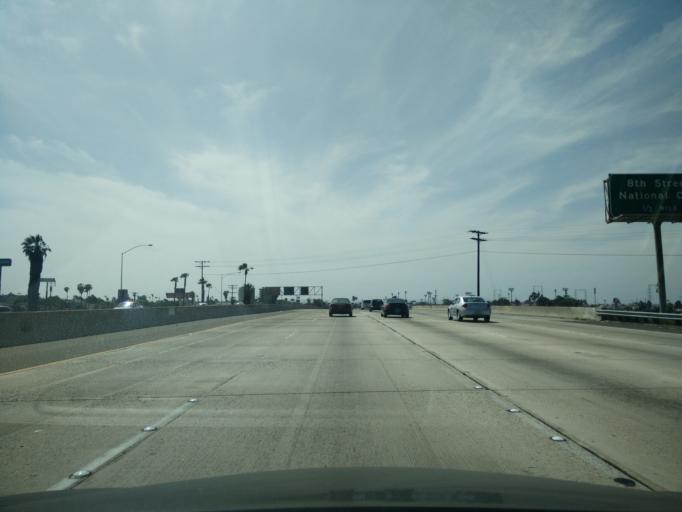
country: US
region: California
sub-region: San Diego County
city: National City
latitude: 32.6838
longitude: -117.1117
